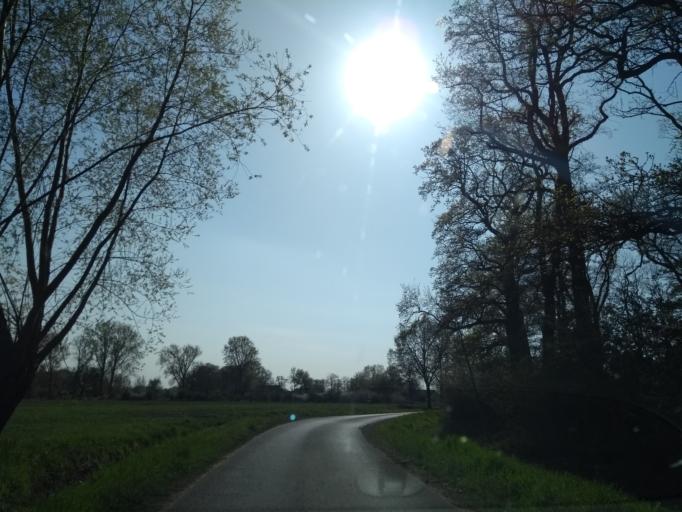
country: DE
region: North Rhine-Westphalia
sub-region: Regierungsbezirk Detmold
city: Delbruck
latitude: 51.7083
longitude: 8.5308
